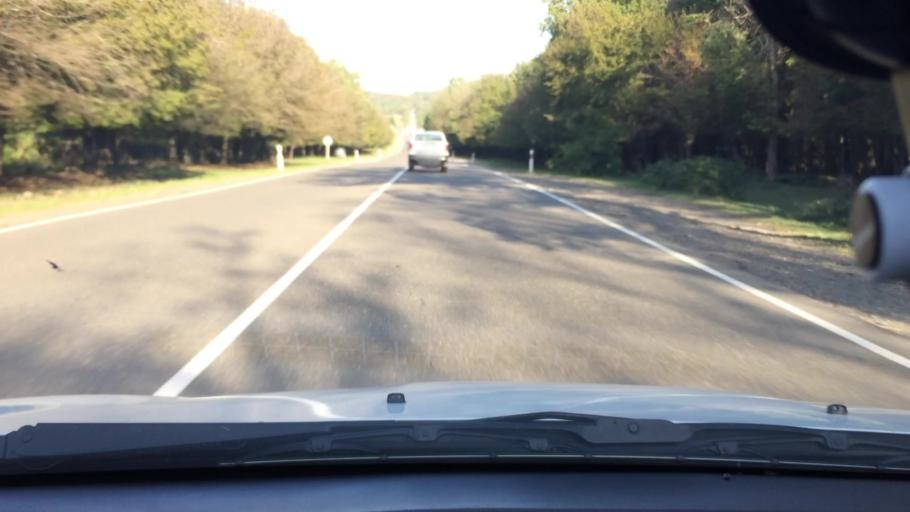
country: GE
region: Imereti
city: Kutaisi
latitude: 42.2348
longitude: 42.7724
